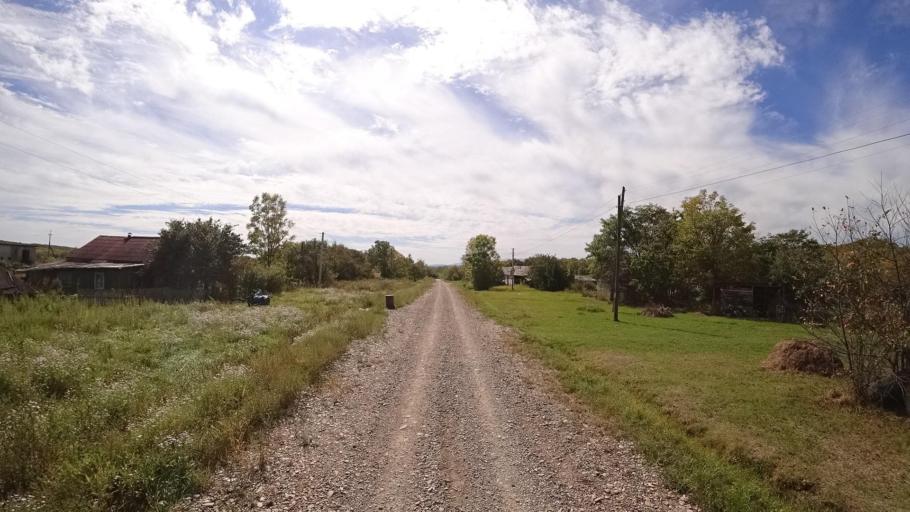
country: RU
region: Primorskiy
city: Yakovlevka
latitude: 44.6400
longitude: 133.5987
